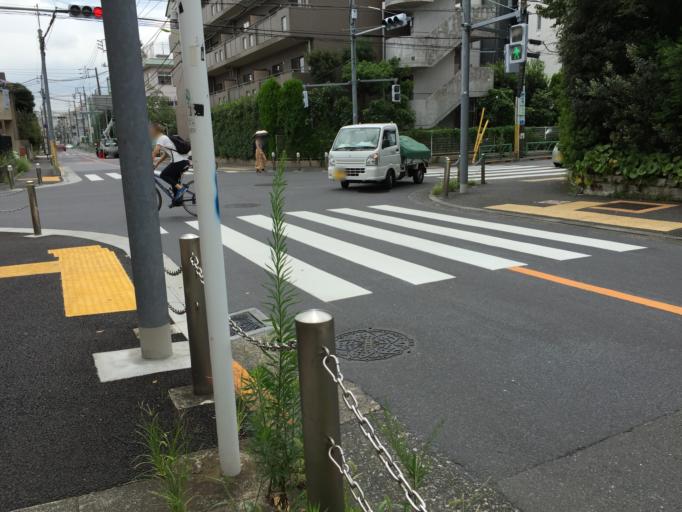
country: JP
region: Tokyo
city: Tokyo
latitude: 35.6572
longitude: 139.6382
